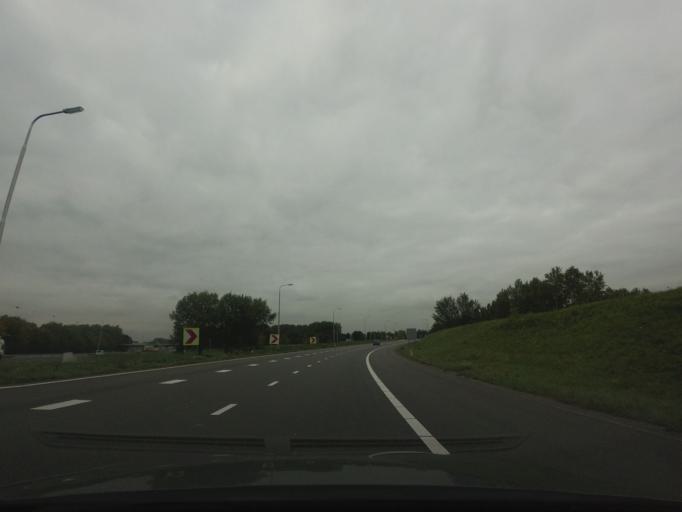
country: NL
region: North Holland
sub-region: Gemeente Landsmeer
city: Landsmeer
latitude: 52.4063
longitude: 4.9444
